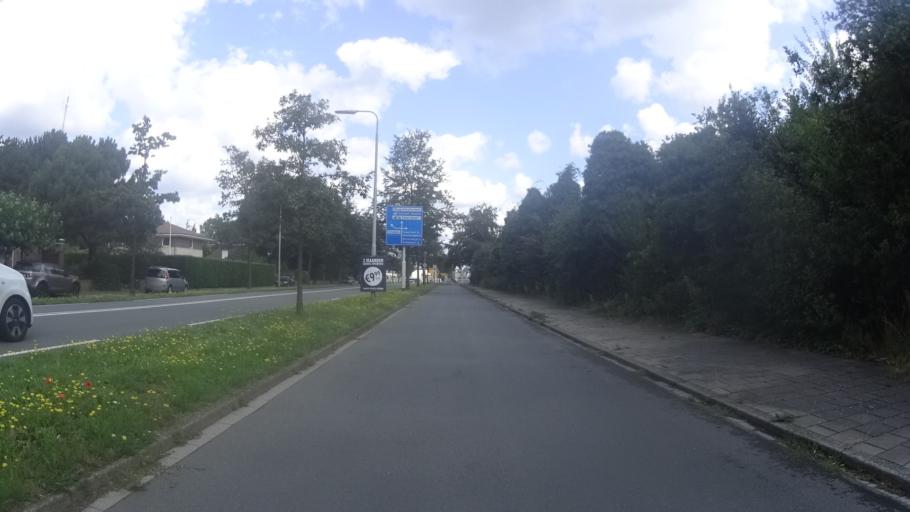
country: NL
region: North Holland
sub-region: Gemeente Velsen
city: Velsen-Zuid
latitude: 52.4600
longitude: 4.6334
